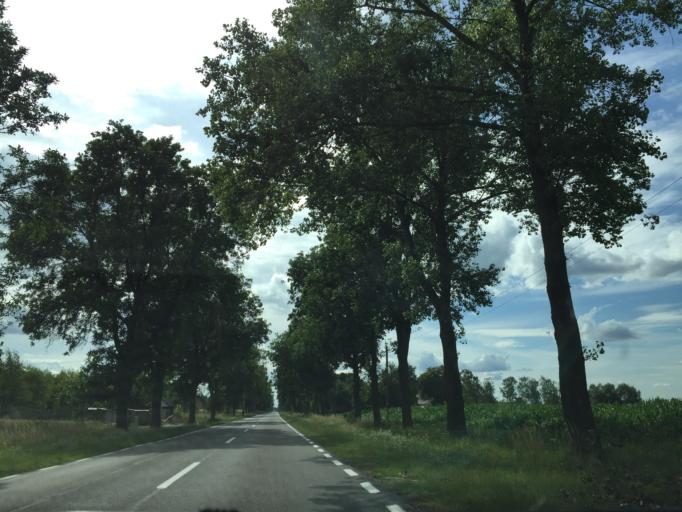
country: PL
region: Lublin Voivodeship
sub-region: Powiat lukowski
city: Trzebieszow
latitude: 51.9872
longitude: 22.6052
